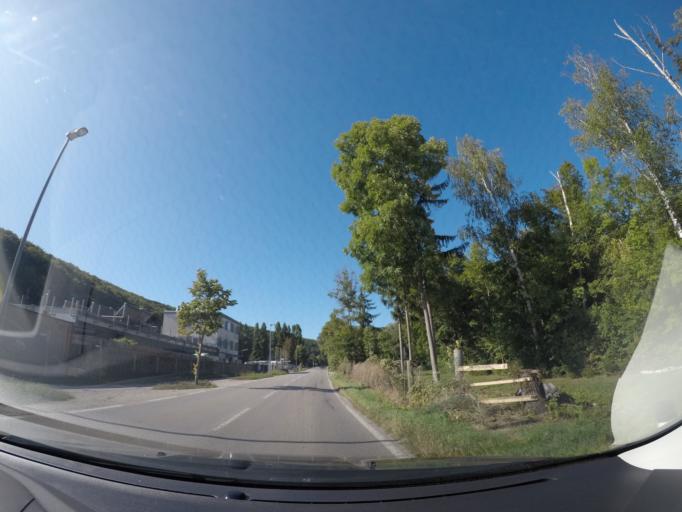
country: AT
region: Lower Austria
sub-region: Politischer Bezirk Modling
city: Kaltenleutgeben
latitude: 48.1426
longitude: 16.1972
